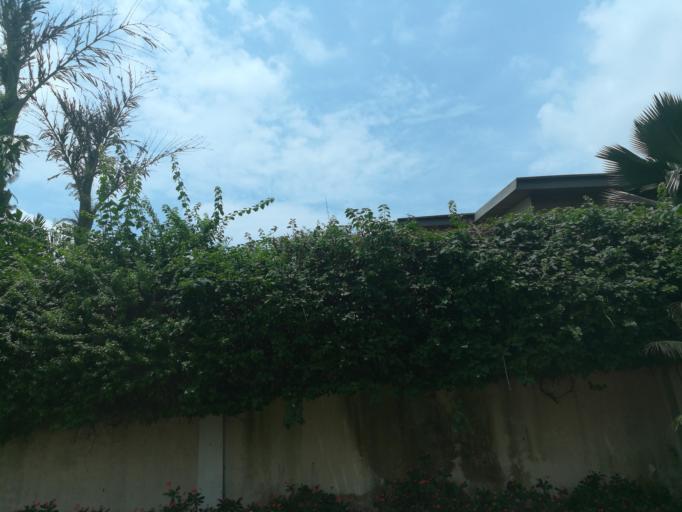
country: NG
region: Lagos
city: Ikeja
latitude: 6.5943
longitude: 3.3601
